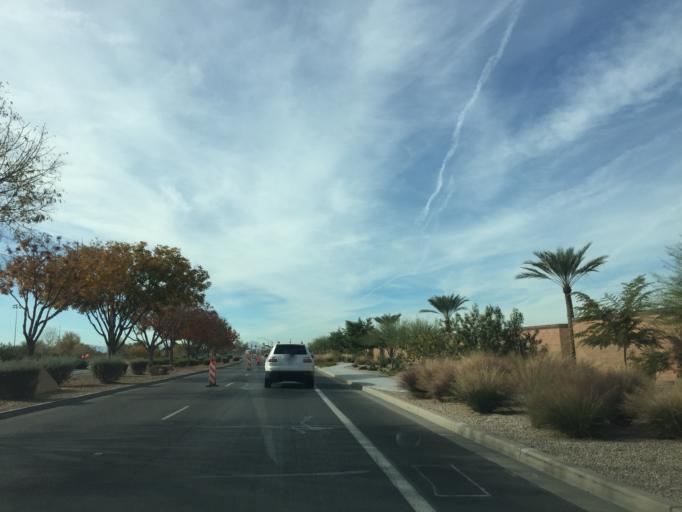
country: US
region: Arizona
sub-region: Maricopa County
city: Chandler
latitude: 33.2769
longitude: -111.8291
